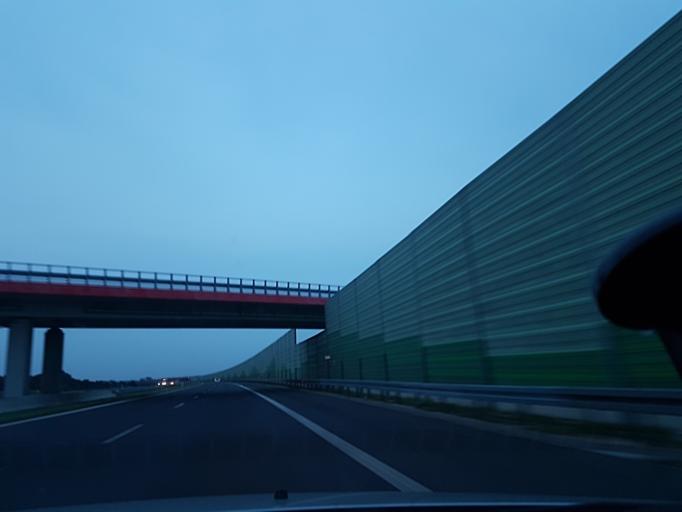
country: PL
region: Lodz Voivodeship
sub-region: Powiat kutnowski
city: Krzyzanow
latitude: 52.1481
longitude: 19.4814
